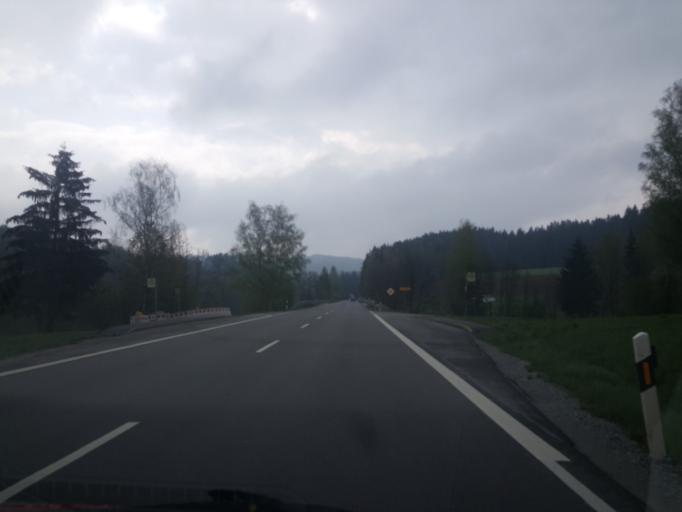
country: DE
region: Bavaria
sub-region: Lower Bavaria
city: Viechtach
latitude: 49.0559
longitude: 12.9149
